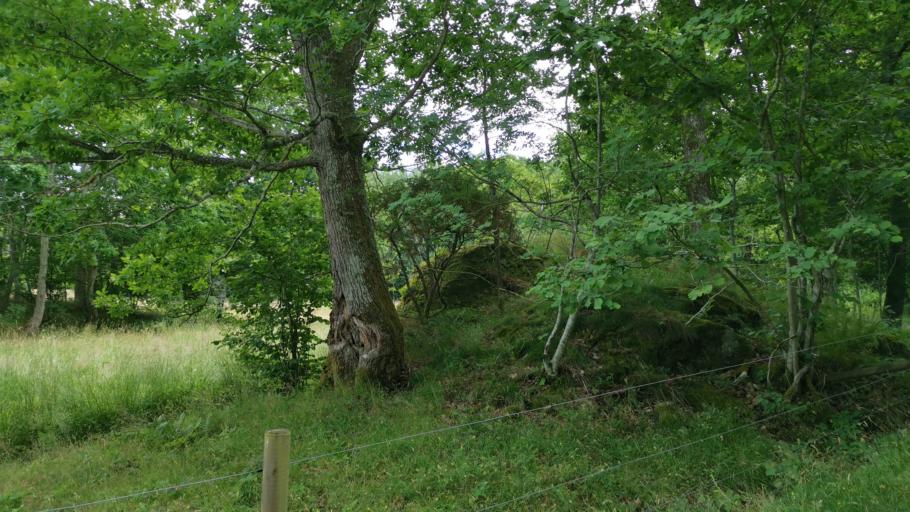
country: SE
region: Vaestra Goetaland
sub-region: Lysekils Kommun
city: Lysekil
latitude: 58.2435
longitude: 11.4850
